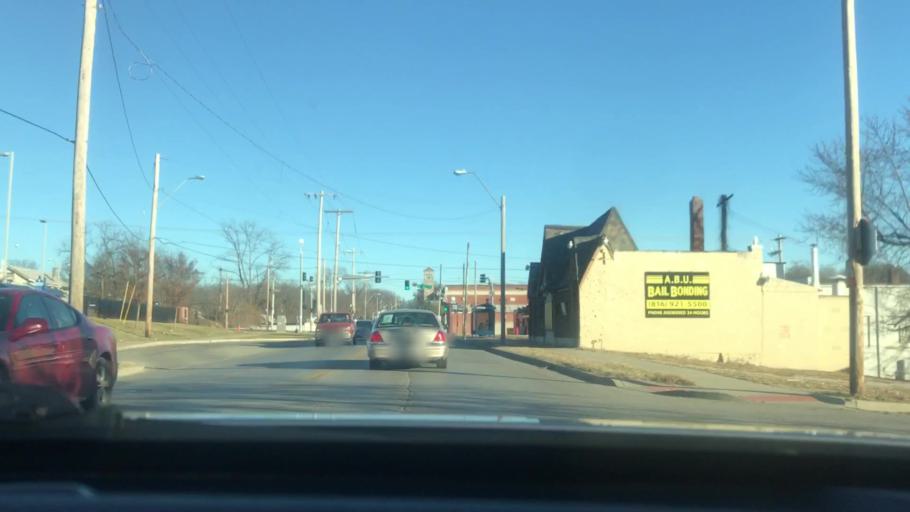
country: US
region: Missouri
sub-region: Jackson County
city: Kansas City
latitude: 39.0555
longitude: -94.5548
